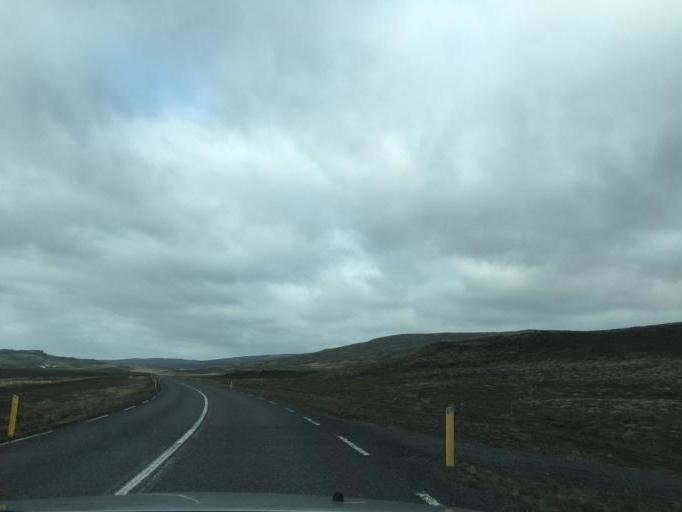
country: IS
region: South
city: Vestmannaeyjar
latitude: 64.2652
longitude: -20.2100
